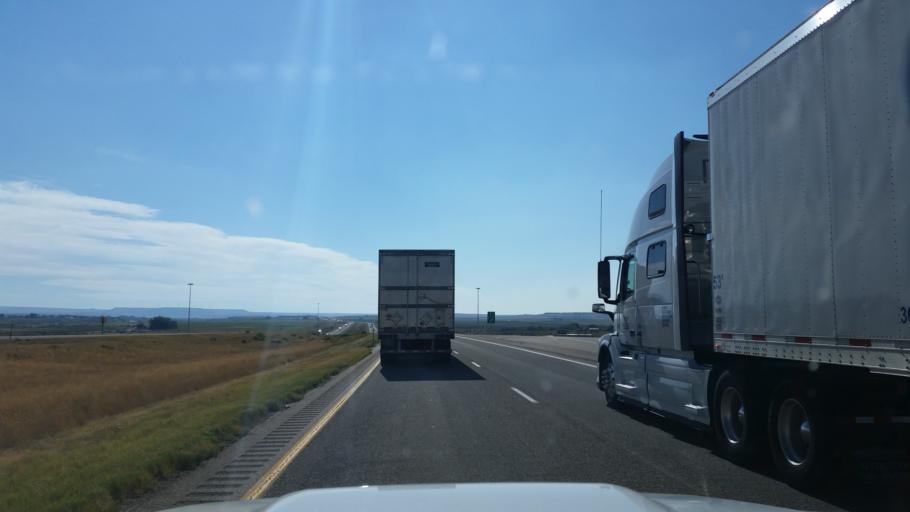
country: US
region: Wyoming
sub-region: Uinta County
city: Lyman
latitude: 41.3681
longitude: -110.2949
